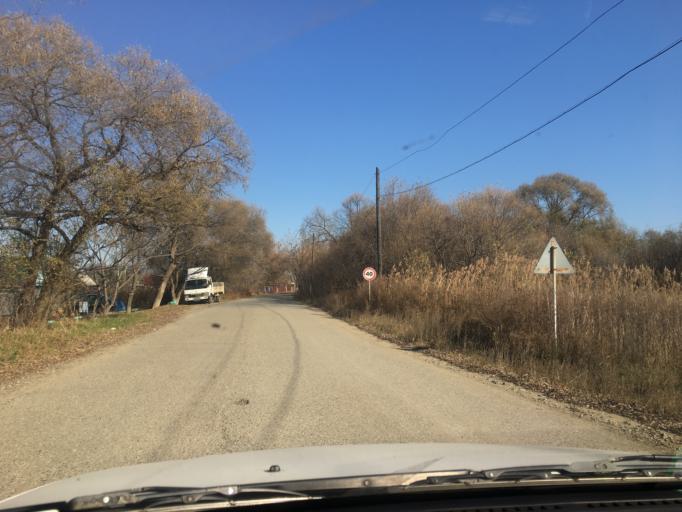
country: RU
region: Primorskiy
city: Dal'nerechensk
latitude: 45.9288
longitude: 133.7093
